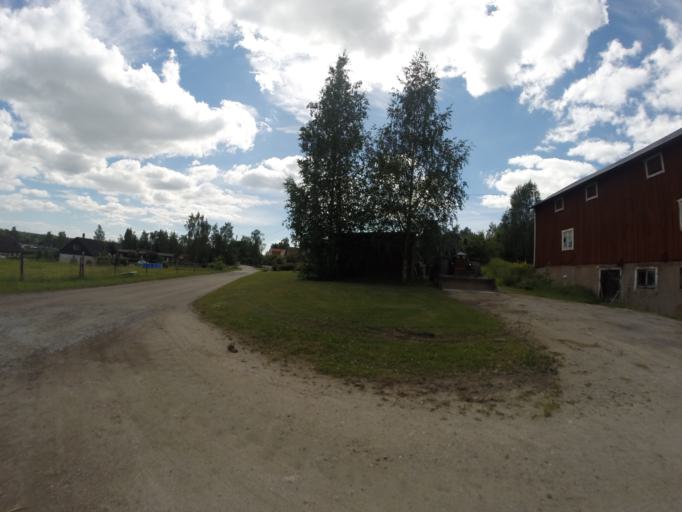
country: SE
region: Soedermanland
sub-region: Eskilstuna Kommun
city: Skogstorp
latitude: 59.3298
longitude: 16.4896
